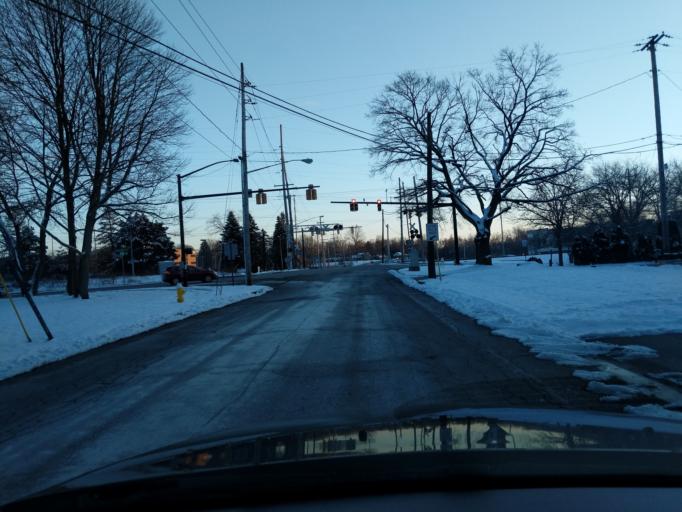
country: US
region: Ohio
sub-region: Summit County
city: Fairlawn
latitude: 41.1105
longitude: -81.5848
